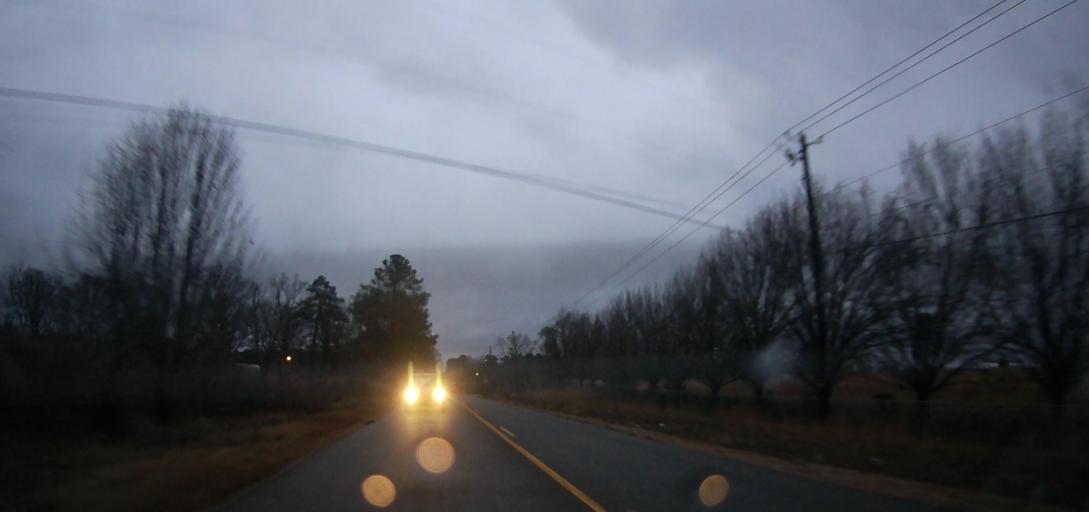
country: US
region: Alabama
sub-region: Tuscaloosa County
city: Vance
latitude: 33.1579
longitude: -87.2299
